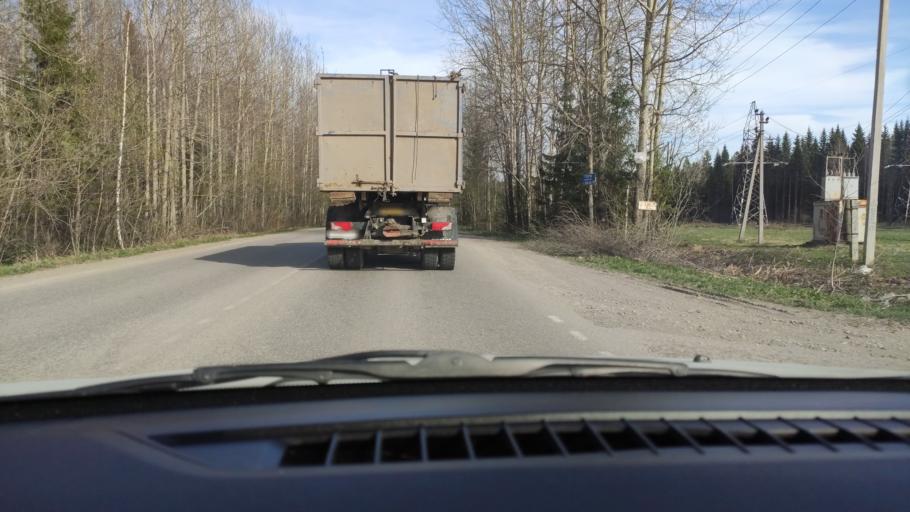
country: RU
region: Perm
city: Ferma
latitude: 57.9380
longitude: 56.4579
